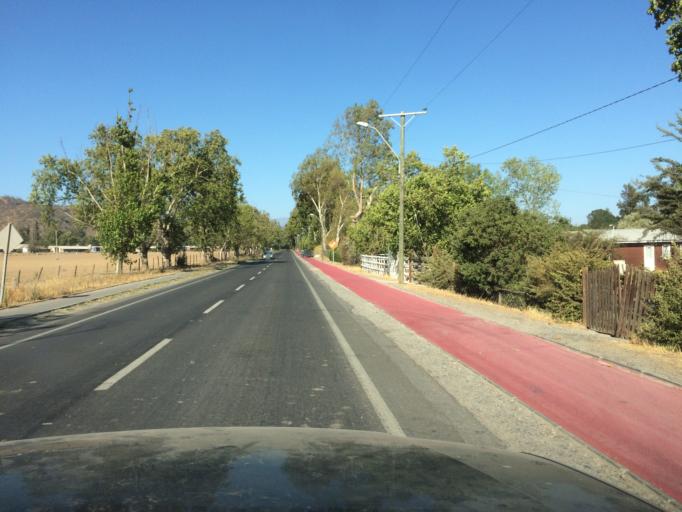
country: CL
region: Santiago Metropolitan
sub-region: Provincia de Melipilla
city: Melipilla
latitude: -33.4915
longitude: -71.1925
